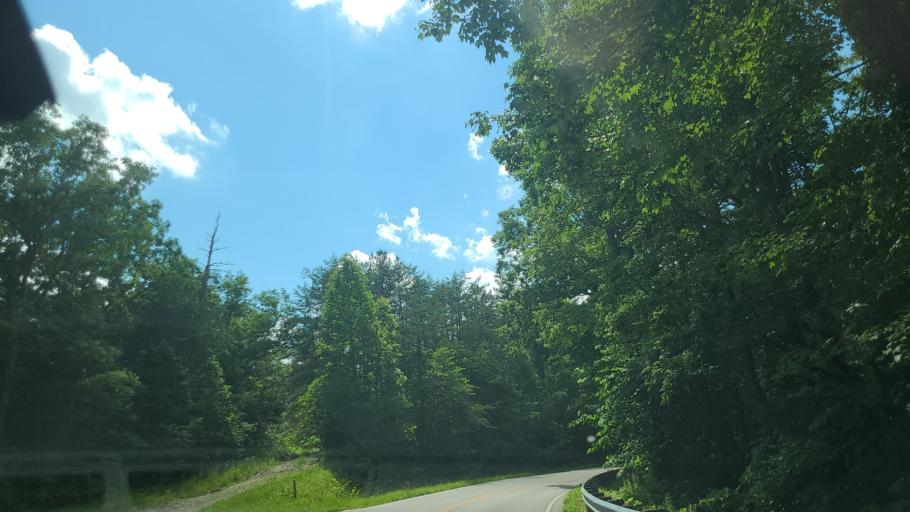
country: US
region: Kentucky
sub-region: Whitley County
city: Williamsburg
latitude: 36.8407
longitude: -84.3022
